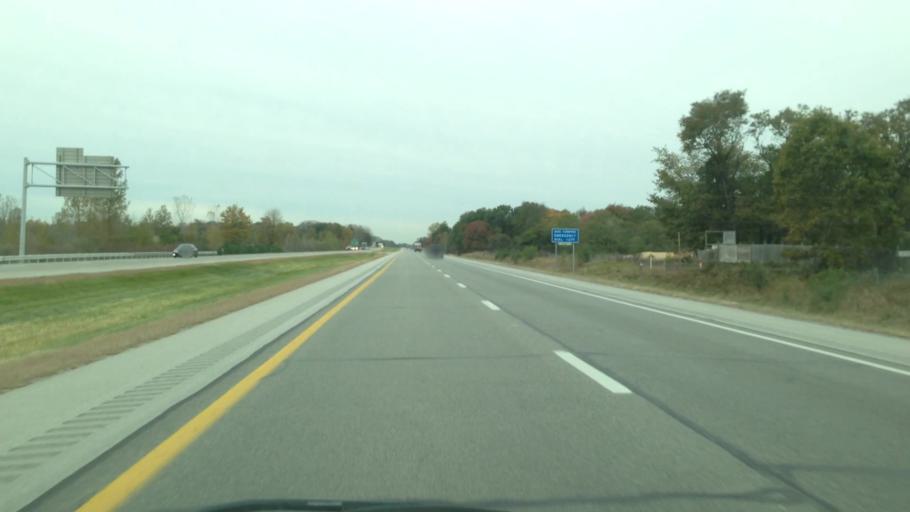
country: US
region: Ohio
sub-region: Fulton County
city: Swanton
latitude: 41.6025
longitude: -83.8152
